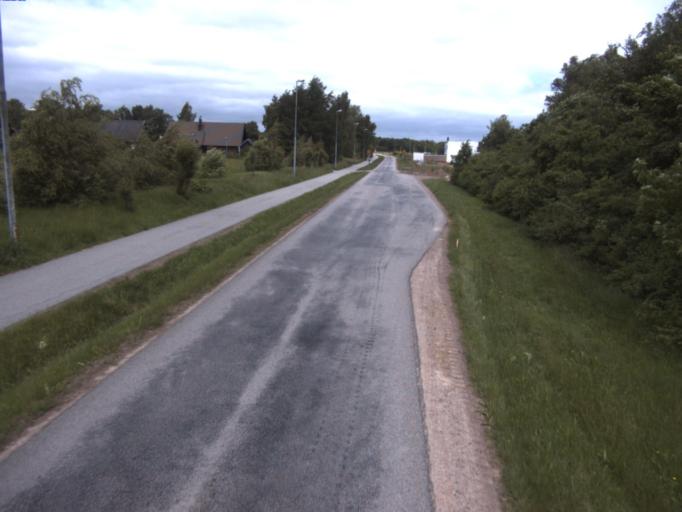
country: SE
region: Skane
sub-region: Helsingborg
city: Odakra
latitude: 56.0576
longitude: 12.7355
